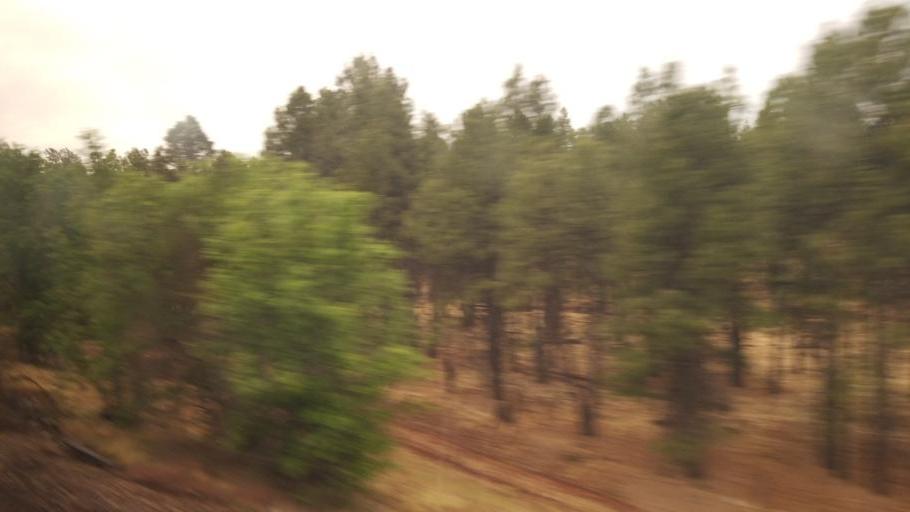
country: US
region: Arizona
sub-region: Coconino County
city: Parks
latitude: 35.2523
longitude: -111.9134
